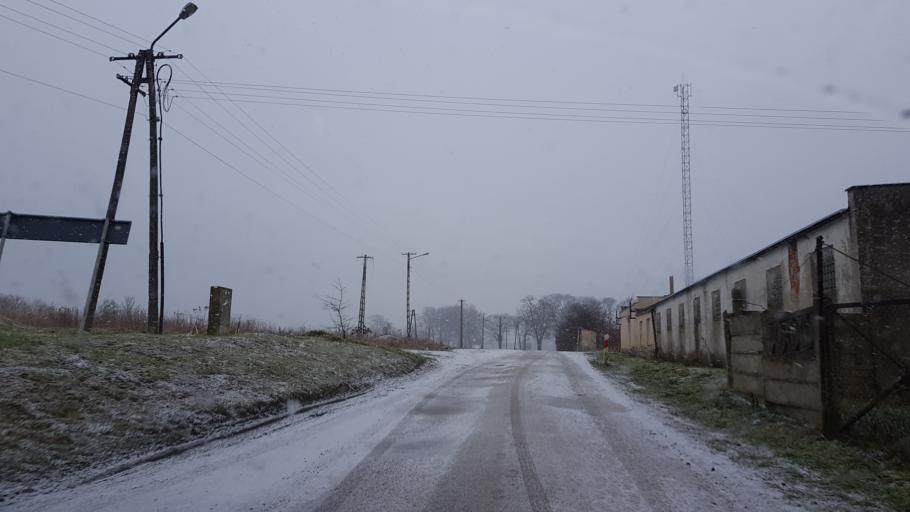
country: PL
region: West Pomeranian Voivodeship
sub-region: Powiat slawienski
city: Slawno
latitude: 54.2731
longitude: 16.6380
